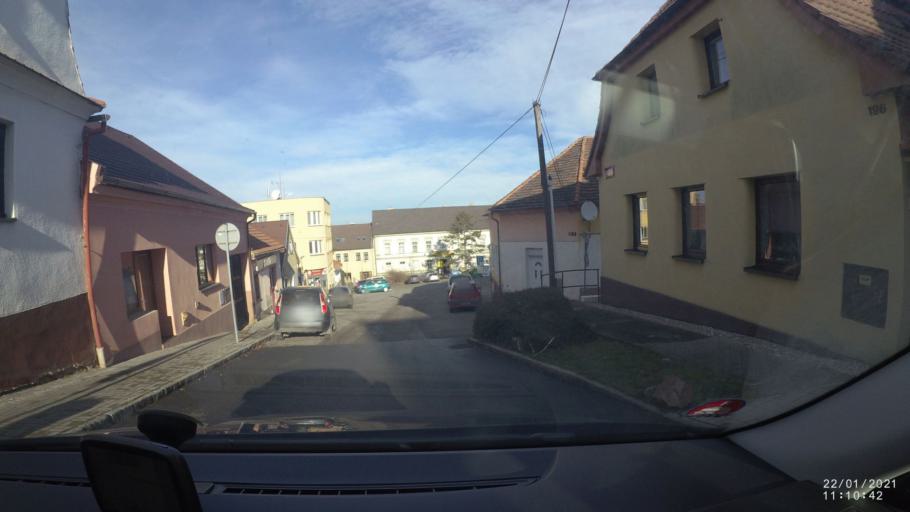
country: CZ
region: Central Bohemia
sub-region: Okres Beroun
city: Horovice
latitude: 49.8374
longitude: 13.9019
